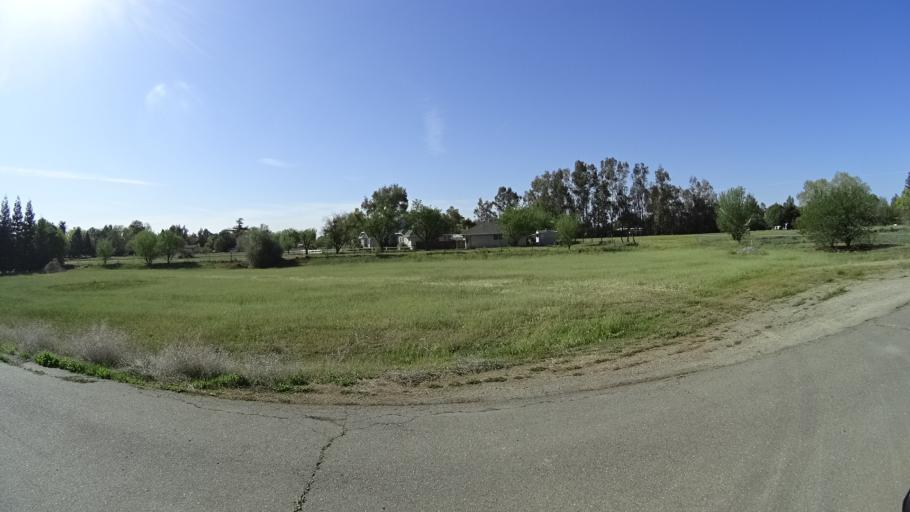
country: US
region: California
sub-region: Glenn County
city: Willows
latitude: 39.5376
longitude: -122.2002
